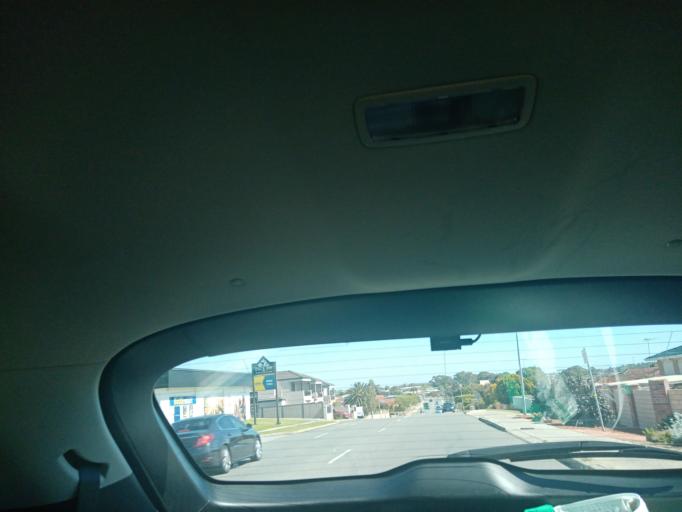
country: AU
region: Western Australia
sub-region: City of Cockburn
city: Spearwood
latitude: -32.1162
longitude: 115.7827
